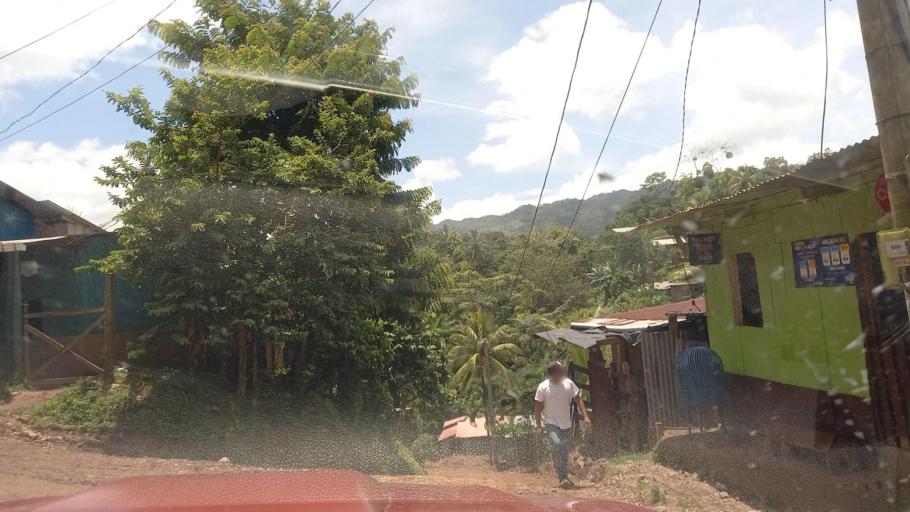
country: NI
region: Atlantico Norte (RAAN)
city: Waslala
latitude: 13.3396
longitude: -85.3705
